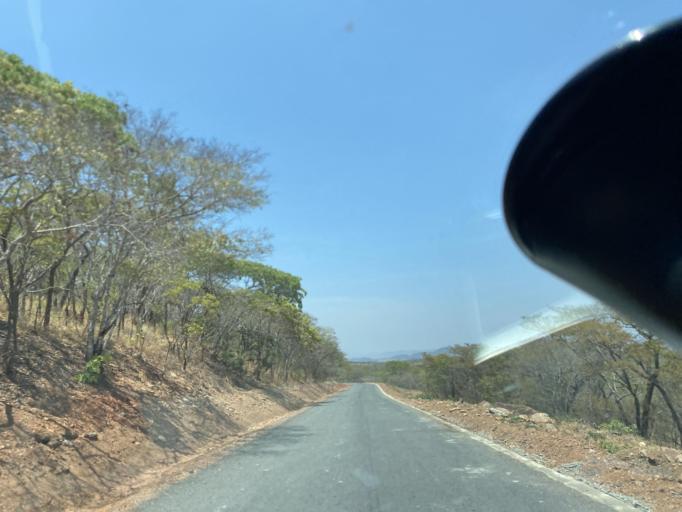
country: ZM
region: Lusaka
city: Kafue
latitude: -15.8540
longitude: 28.4187
